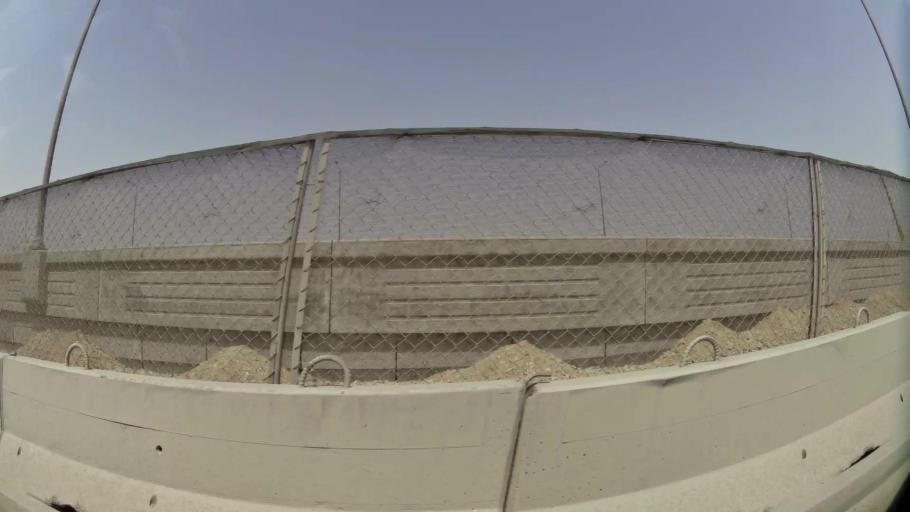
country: QA
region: Al Wakrah
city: Al Wukayr
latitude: 25.1939
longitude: 51.4591
